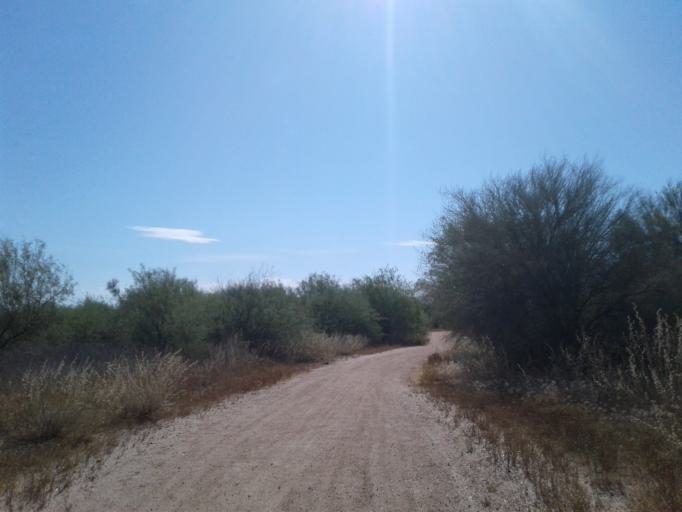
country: US
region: Arizona
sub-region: Maricopa County
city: Paradise Valley
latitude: 33.6791
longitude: -112.0223
